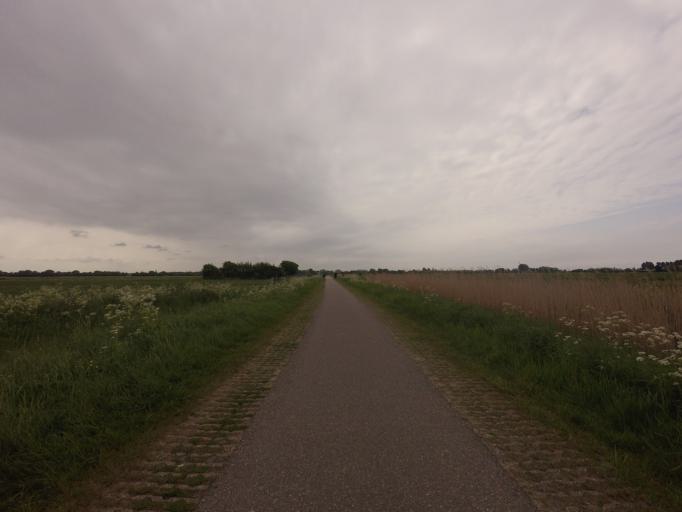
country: NL
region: Zeeland
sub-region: Gemeente Middelburg
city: Middelburg
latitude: 51.5172
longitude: 3.5880
